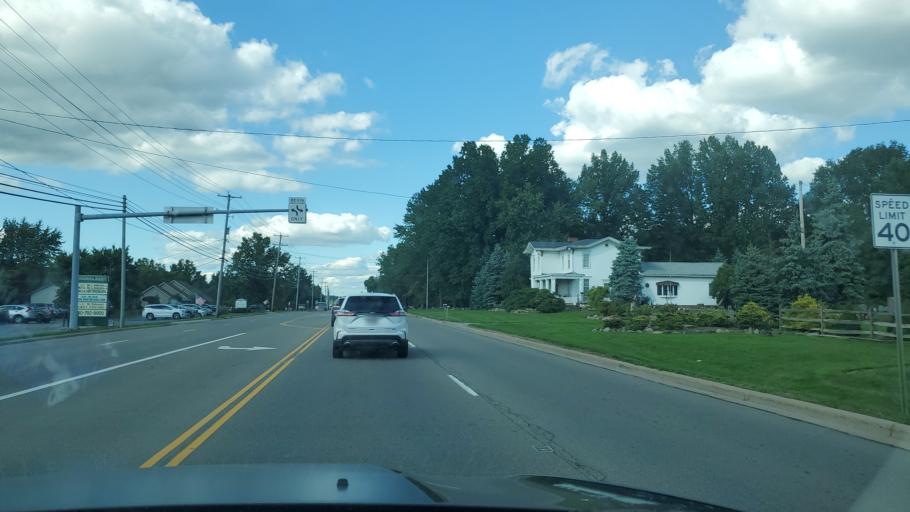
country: US
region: Ohio
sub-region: Mahoning County
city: Austintown
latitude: 41.0885
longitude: -80.7631
